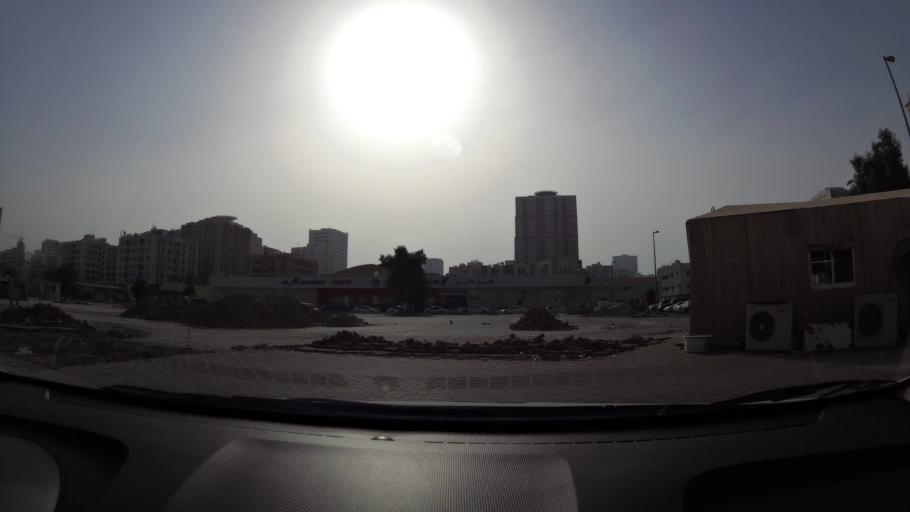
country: AE
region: Ash Shariqah
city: Sharjah
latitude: 25.3392
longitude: 55.4011
